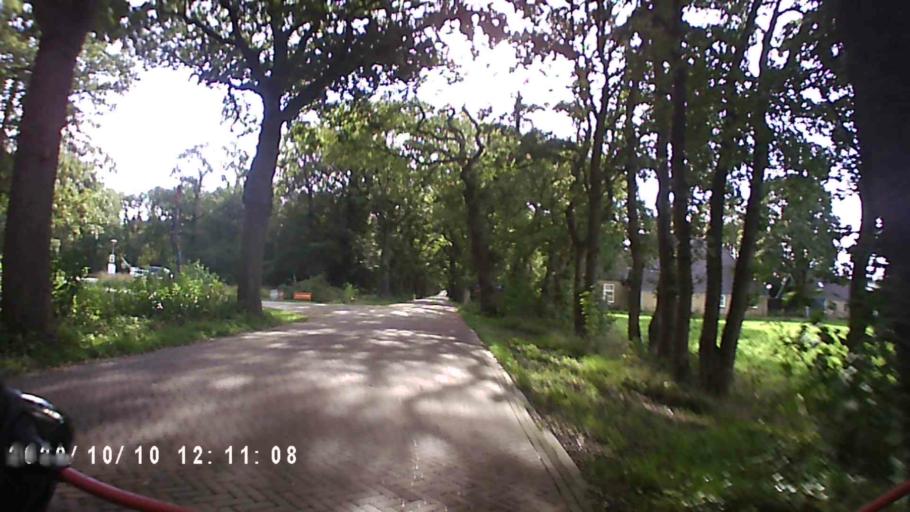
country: NL
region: Friesland
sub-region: Gemeente Heerenveen
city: Jubbega
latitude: 53.0408
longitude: 6.1490
